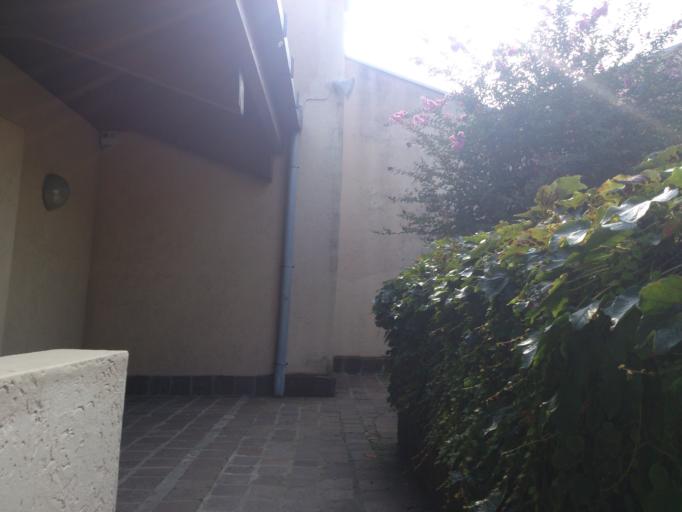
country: IT
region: Lombardy
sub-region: Citta metropolitana di Milano
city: San Donato Milanese
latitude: 45.4147
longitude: 9.2651
